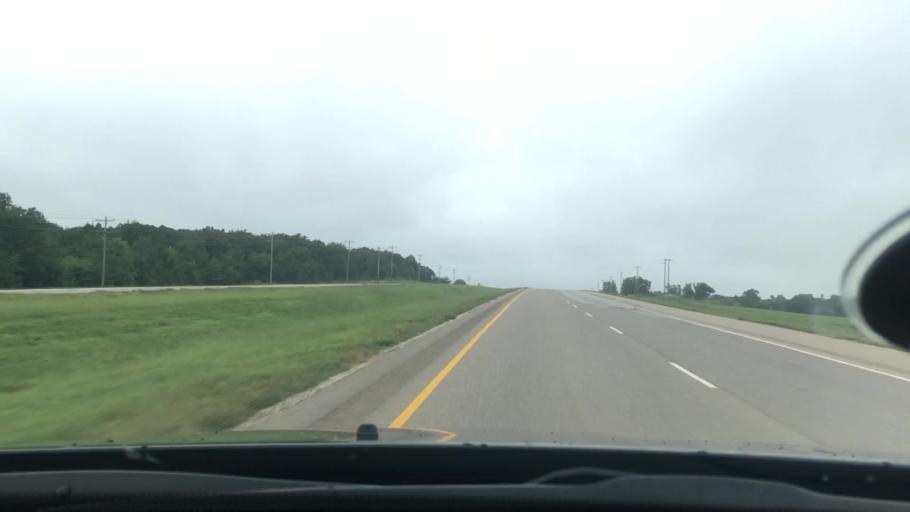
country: US
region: Oklahoma
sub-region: Seminole County
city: Seminole
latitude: 35.3288
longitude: -96.6713
